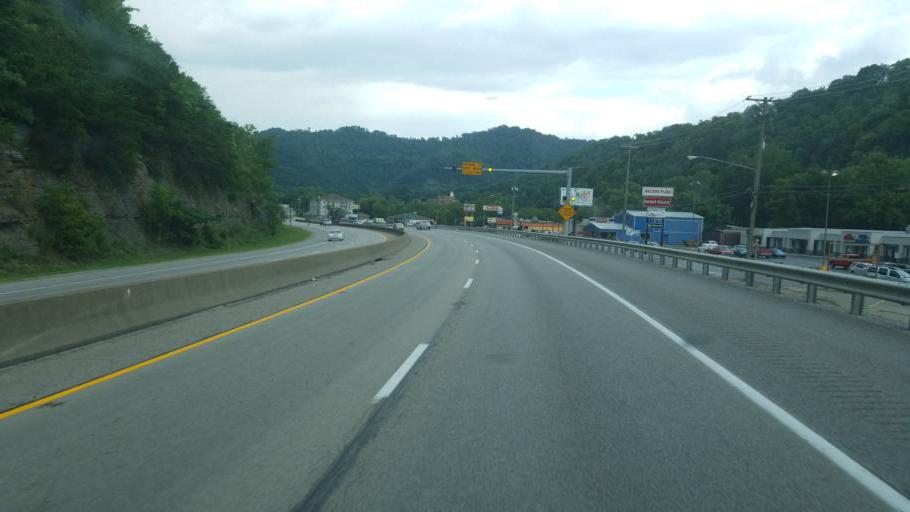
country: US
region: Kentucky
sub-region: Pike County
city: Pikeville
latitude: 37.4672
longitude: -82.5319
